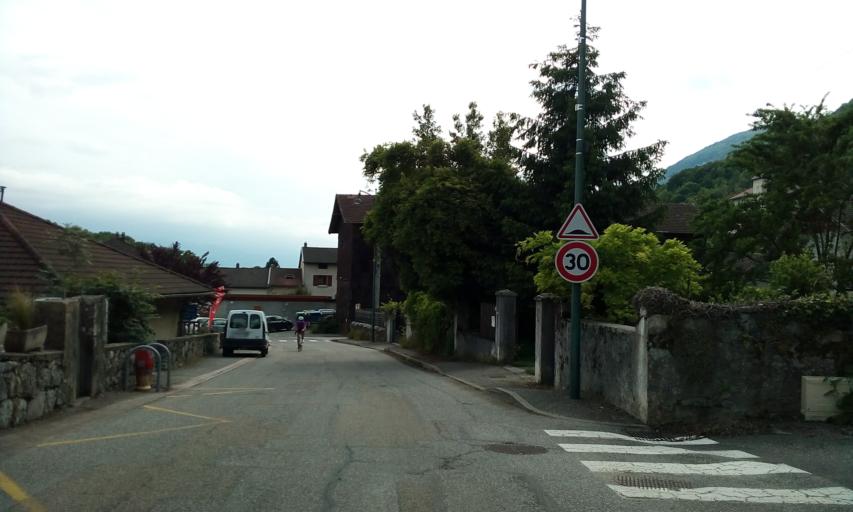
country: FR
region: Rhone-Alpes
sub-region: Departement de l'Isere
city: Saint-Vincent-de-Mercuze
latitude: 45.3985
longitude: 5.9628
